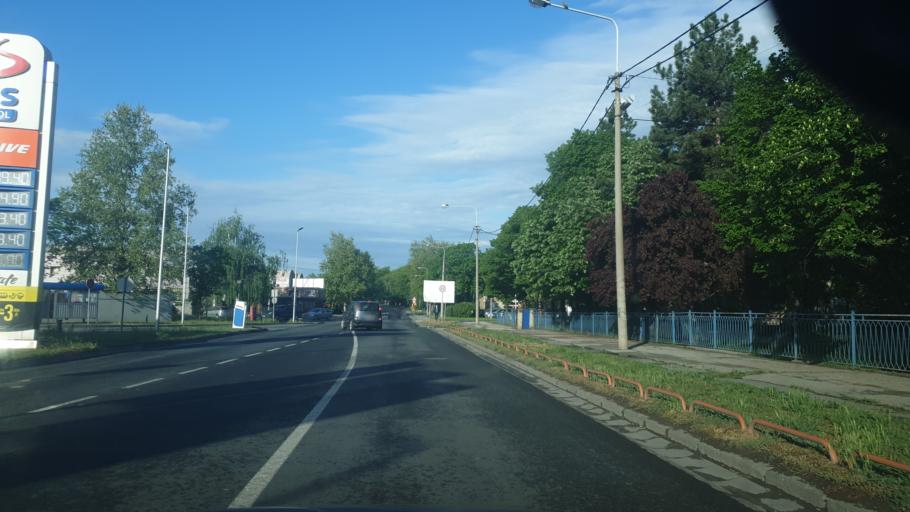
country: RS
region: Central Serbia
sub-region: Belgrade
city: Obrenovac
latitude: 44.6506
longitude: 20.1932
